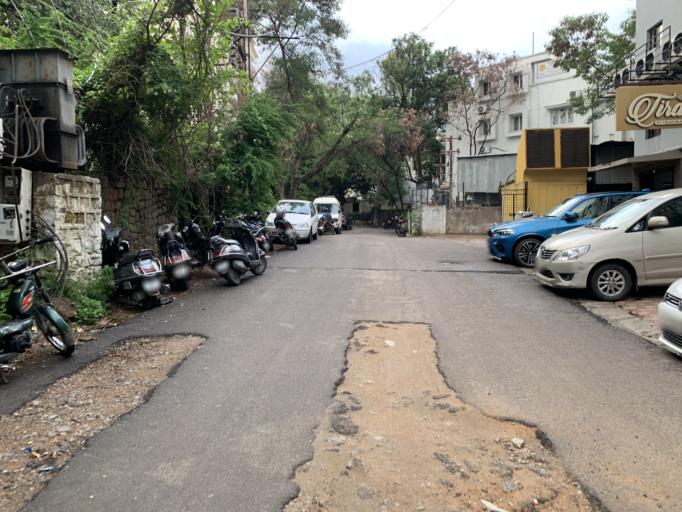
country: IN
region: Telangana
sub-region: Hyderabad
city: Hyderabad
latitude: 17.4260
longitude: 78.4351
